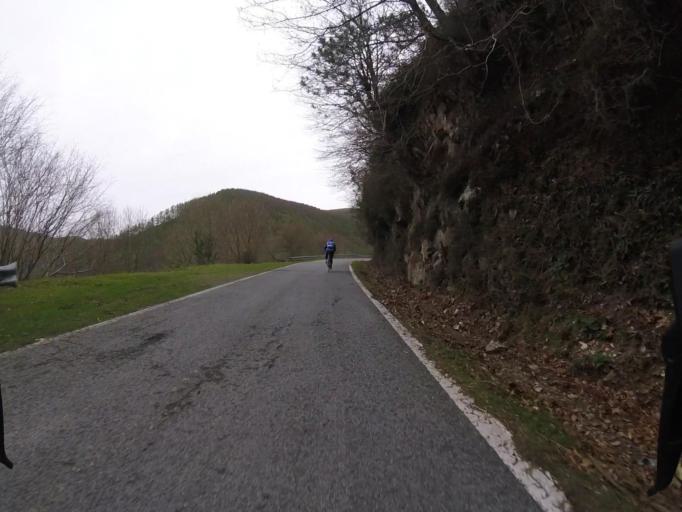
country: ES
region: Basque Country
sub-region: Provincia de Guipuzcoa
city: Irun
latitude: 43.2739
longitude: -1.7841
